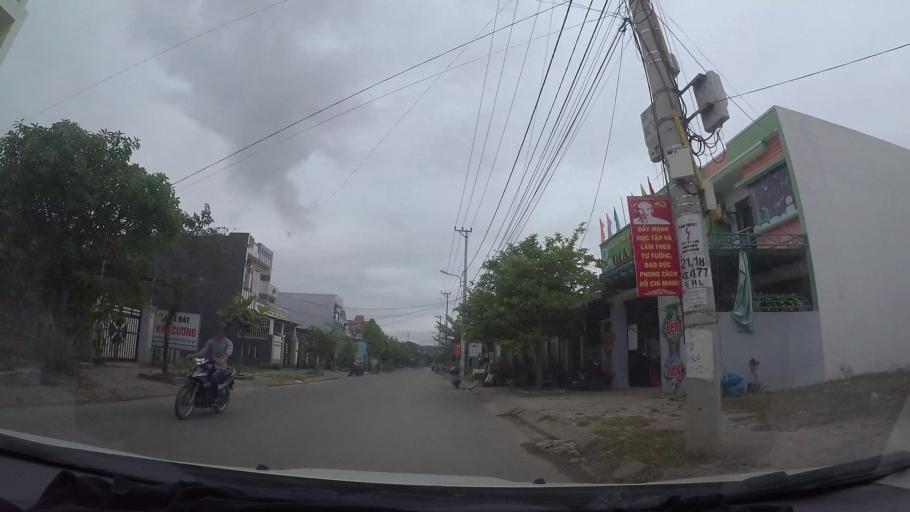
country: VN
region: Da Nang
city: Lien Chieu
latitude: 16.0941
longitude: 108.1039
